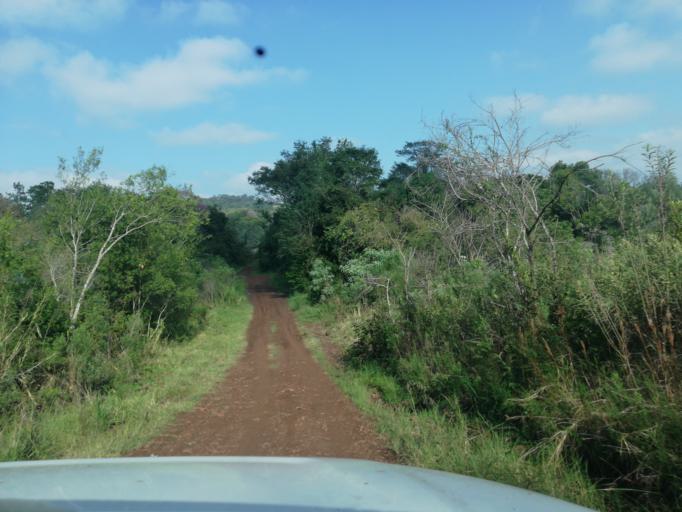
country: AR
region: Misiones
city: Cerro Azul
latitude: -27.6010
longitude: -55.5308
